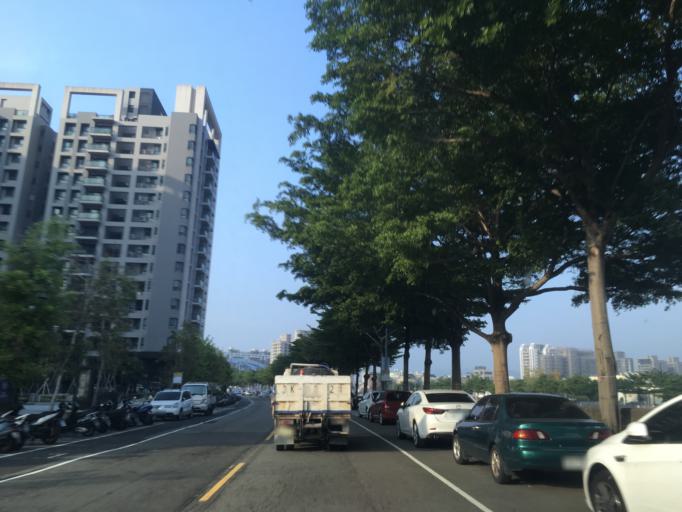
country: TW
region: Taiwan
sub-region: Taichung City
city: Taichung
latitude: 24.1555
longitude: 120.7031
